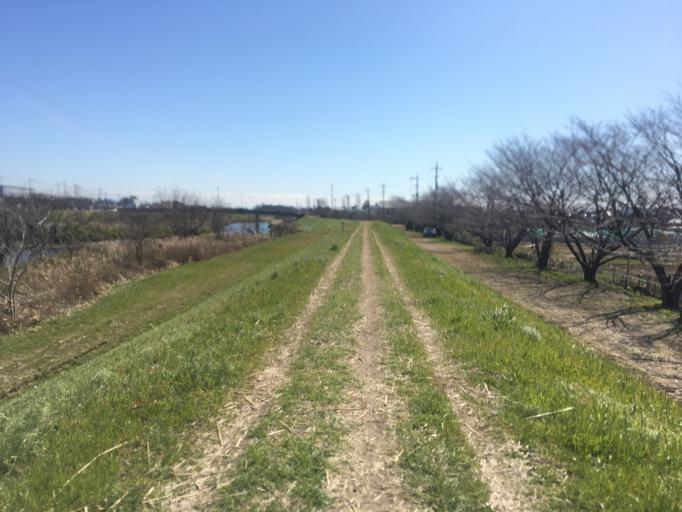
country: JP
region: Saitama
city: Asaka
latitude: 35.8221
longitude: 139.6039
